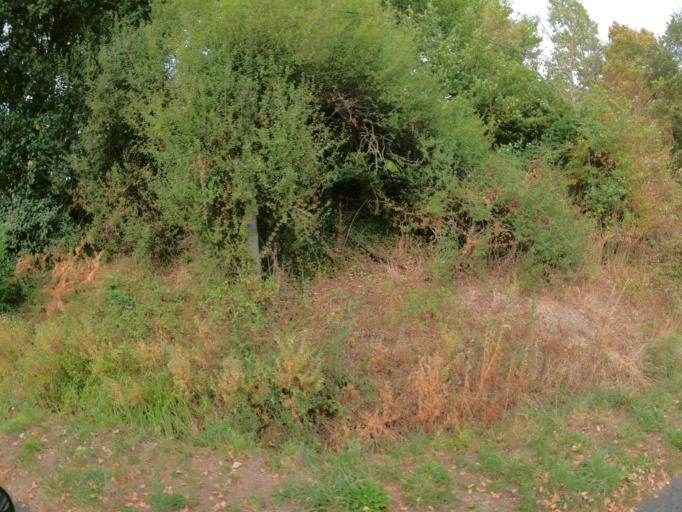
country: FR
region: Pays de la Loire
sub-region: Departement de Maine-et-Loire
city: La Seguiniere
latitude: 47.0638
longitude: -0.9327
